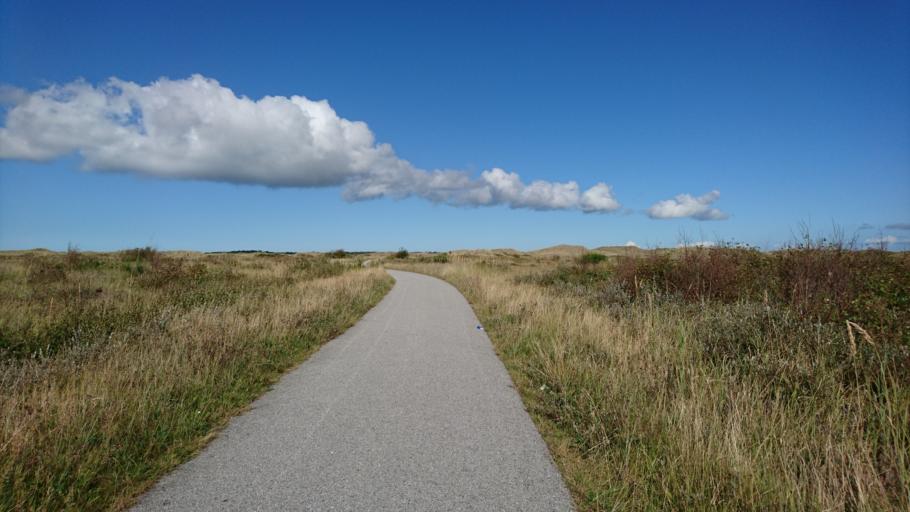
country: DK
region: North Denmark
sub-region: Frederikshavn Kommune
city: Skagen
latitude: 57.6796
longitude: 10.5029
